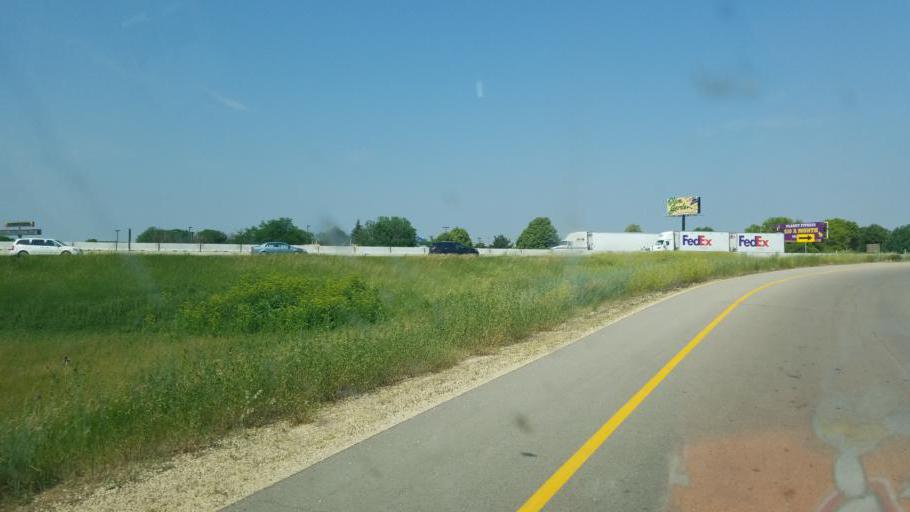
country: US
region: Wisconsin
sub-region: Rock County
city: Janesville
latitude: 42.7188
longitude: -88.9842
